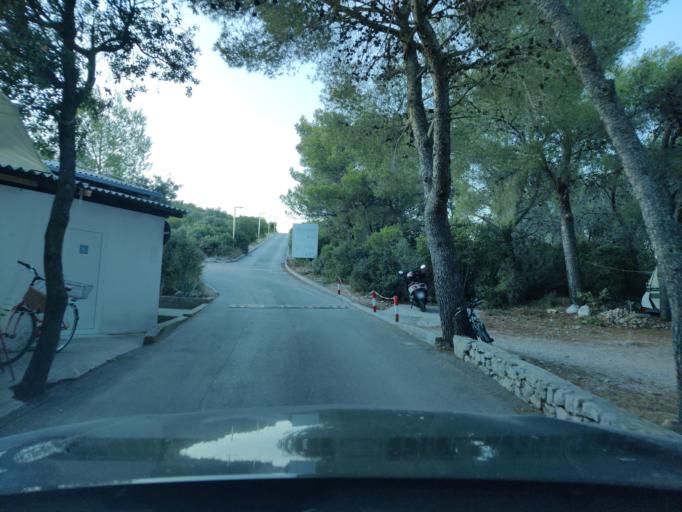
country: HR
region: Sibensko-Kniniska
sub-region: Grad Sibenik
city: Tisno
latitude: 43.8094
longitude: 15.6284
